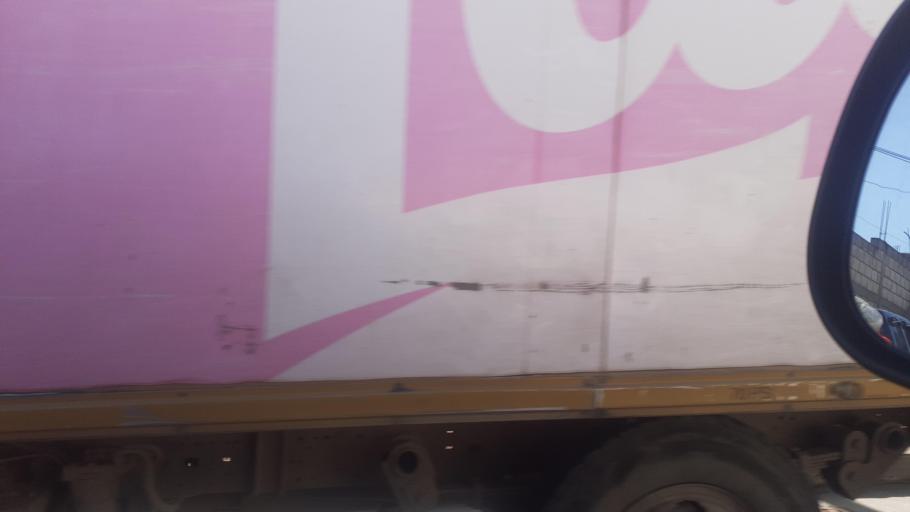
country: GT
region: Quetzaltenango
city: Cantel
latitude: 14.8158
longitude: -91.4507
